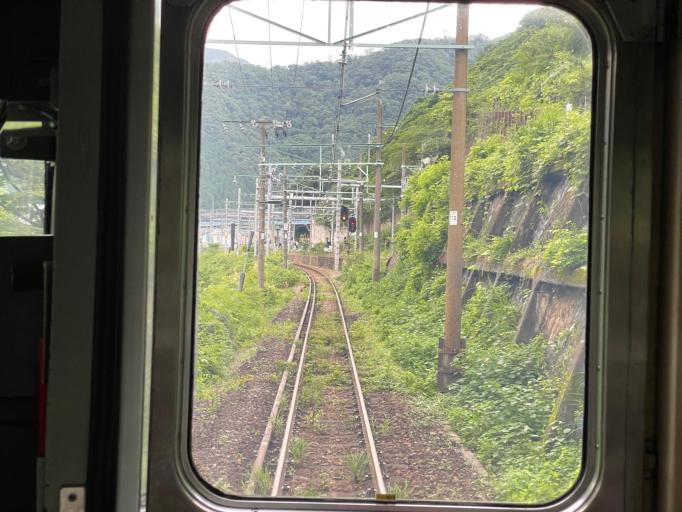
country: JP
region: Gunma
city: Numata
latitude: 36.7730
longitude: 138.9711
